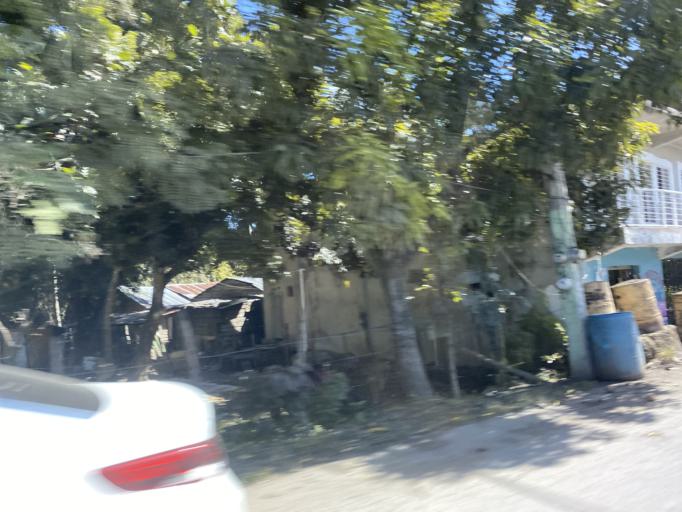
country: DO
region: Puerto Plata
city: Imbert
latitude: 19.8105
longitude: -70.7791
